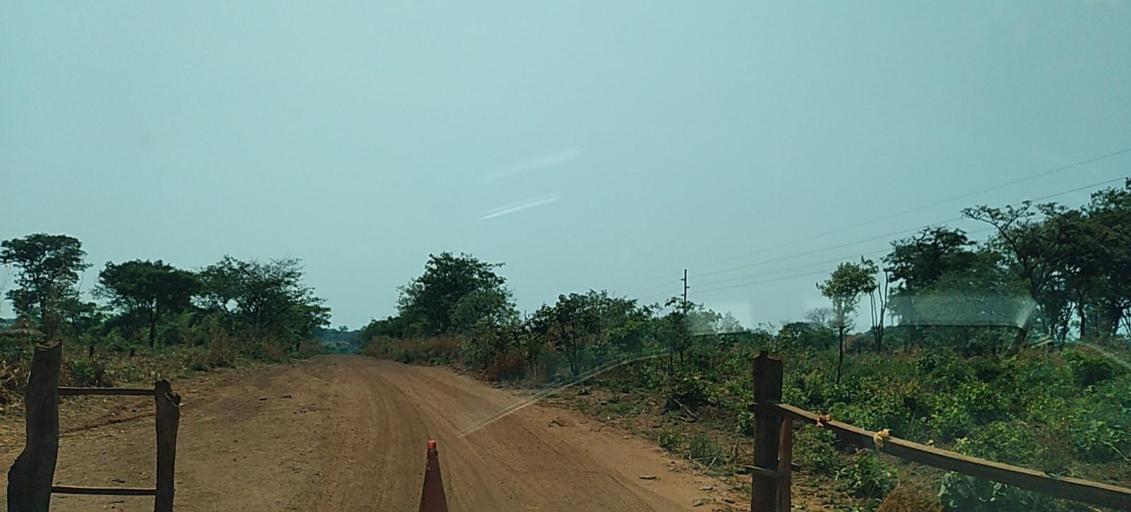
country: ZM
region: North-Western
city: Kansanshi
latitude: -12.0063
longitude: 26.5289
